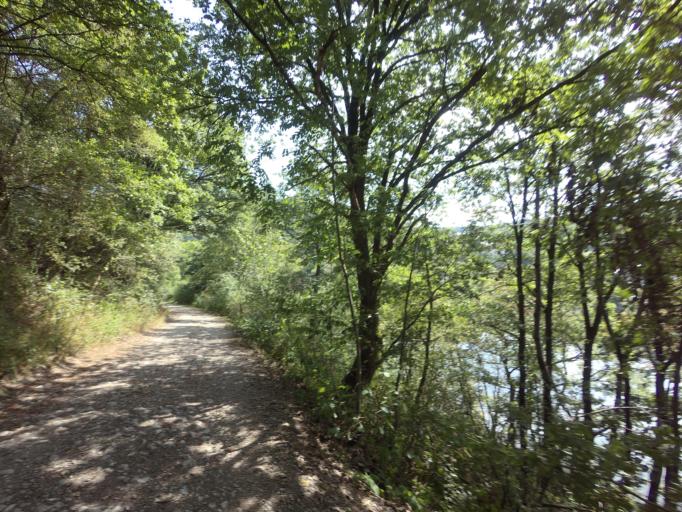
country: DE
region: North Rhine-Westphalia
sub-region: Regierungsbezirk Koln
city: Simmerath
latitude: 50.5878
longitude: 6.3793
